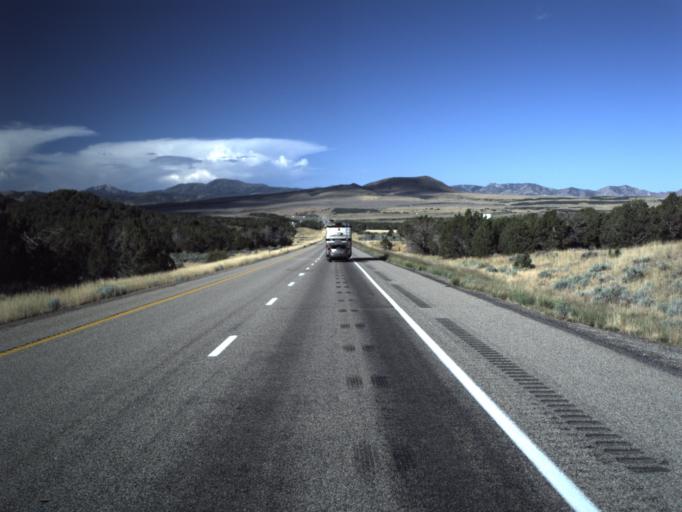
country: US
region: Utah
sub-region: Beaver County
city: Beaver
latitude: 38.6022
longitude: -112.5552
